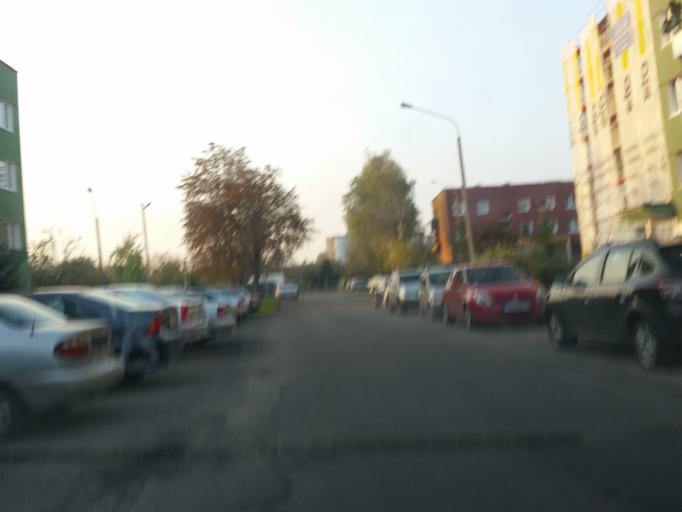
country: PL
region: Silesian Voivodeship
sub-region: Sosnowiec
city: Sosnowiec
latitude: 50.2708
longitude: 19.1184
